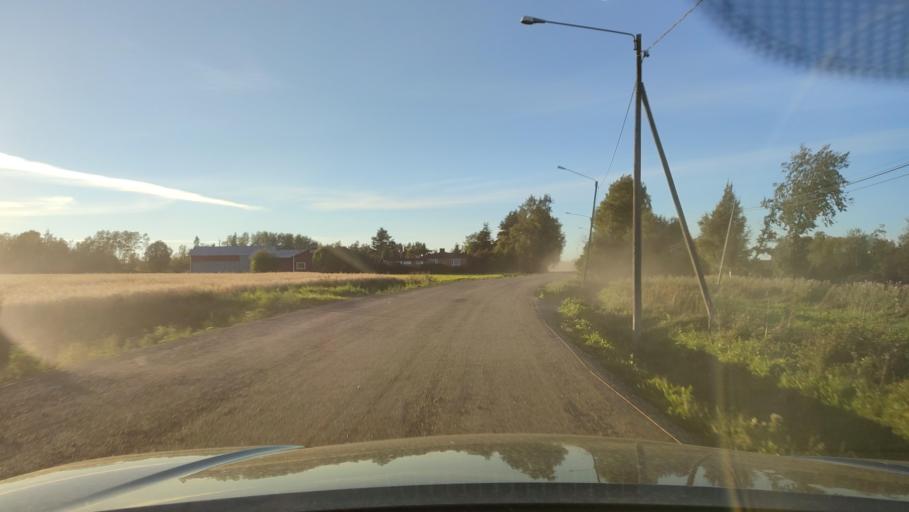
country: FI
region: Southern Ostrobothnia
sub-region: Suupohja
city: Karijoki
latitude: 62.2470
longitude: 21.5561
